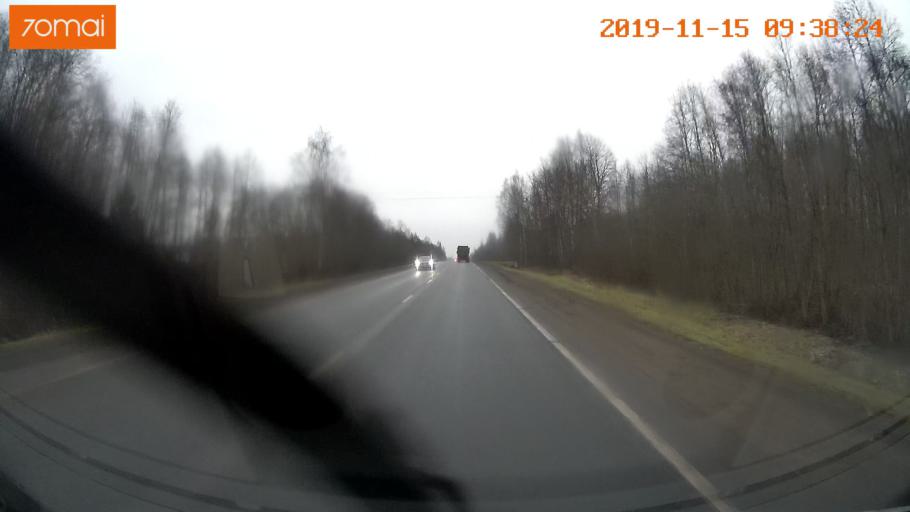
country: RU
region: Vologda
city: Sheksna
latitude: 59.2322
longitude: 38.4550
